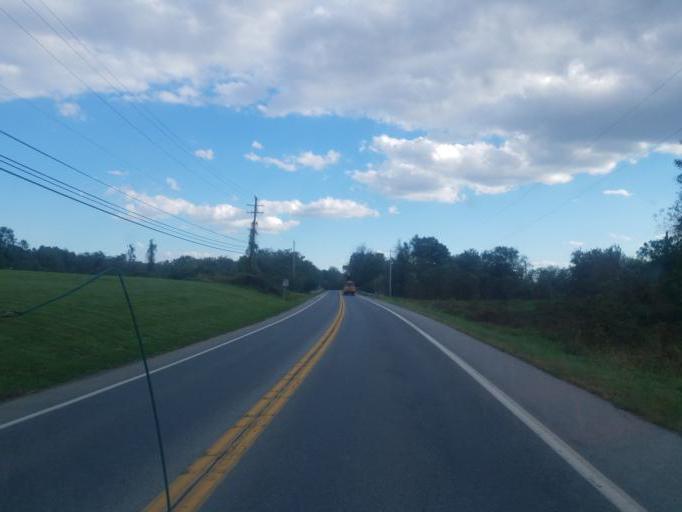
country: US
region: Pennsylvania
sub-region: Dauphin County
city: Middletown
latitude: 40.1697
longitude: -76.7226
